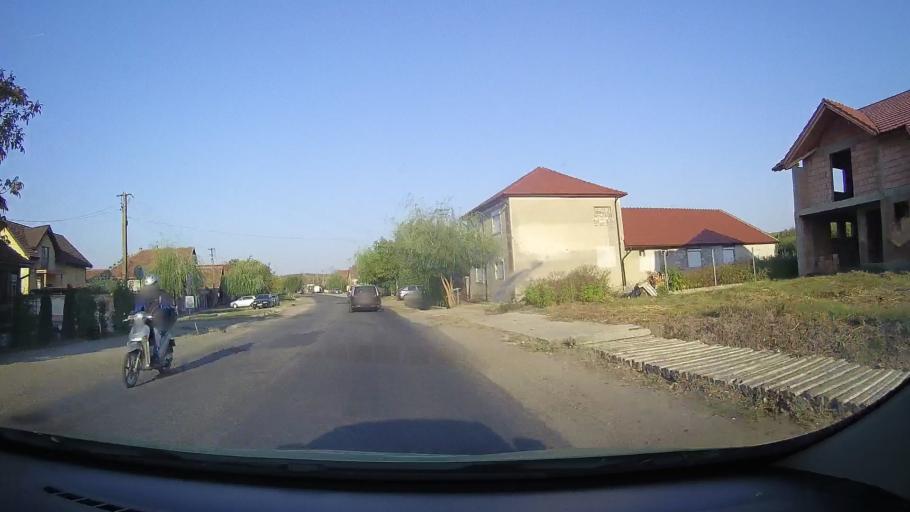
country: RO
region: Arad
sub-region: Comuna Siria
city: Galsa
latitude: 46.2933
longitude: 21.6659
